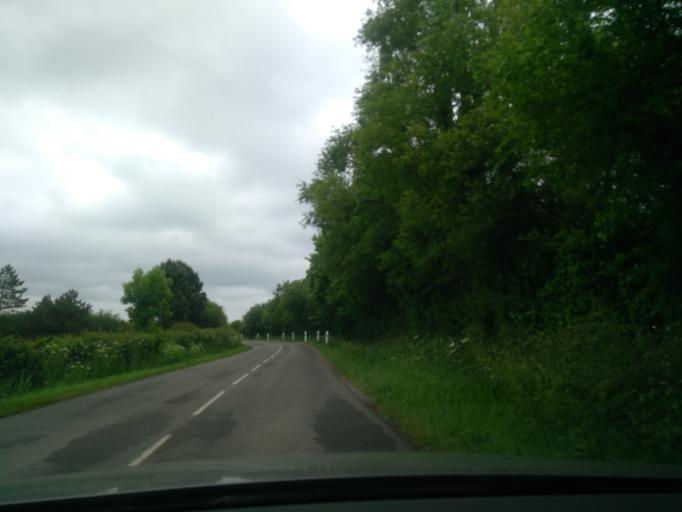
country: FR
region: Lower Normandy
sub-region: Departement de la Manche
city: Sainte-Mere-Eglise
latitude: 49.4668
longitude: -1.2561
